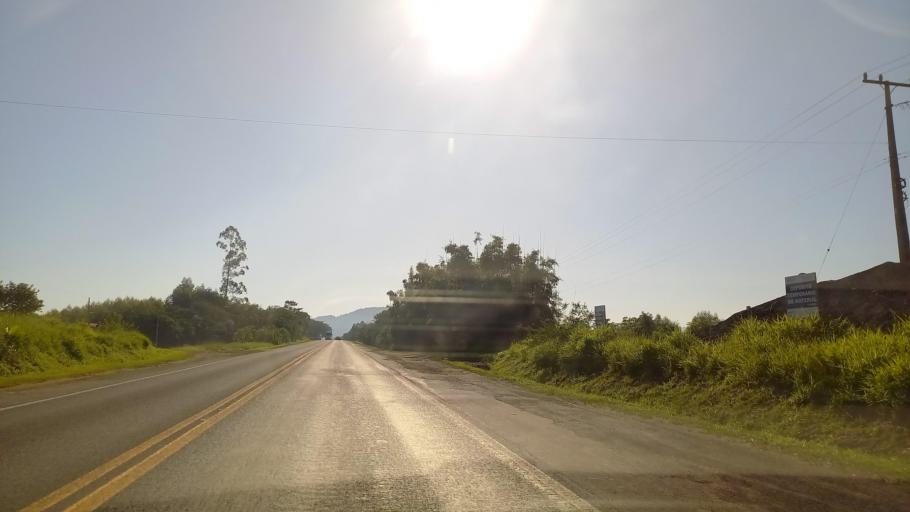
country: BR
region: Rio Grande do Sul
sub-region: Taquari
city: Taquari
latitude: -29.6973
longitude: -51.7497
